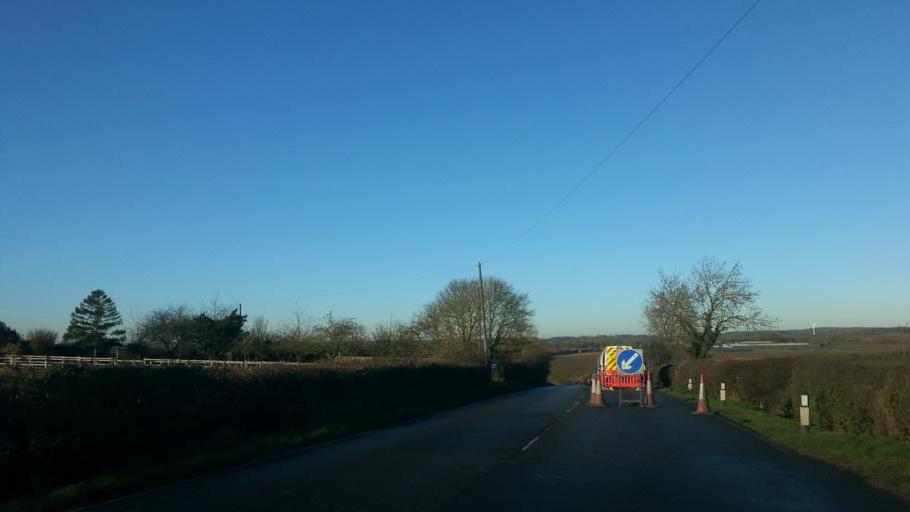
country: GB
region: England
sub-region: Nottinghamshire
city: Southwell
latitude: 53.0947
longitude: -0.9120
